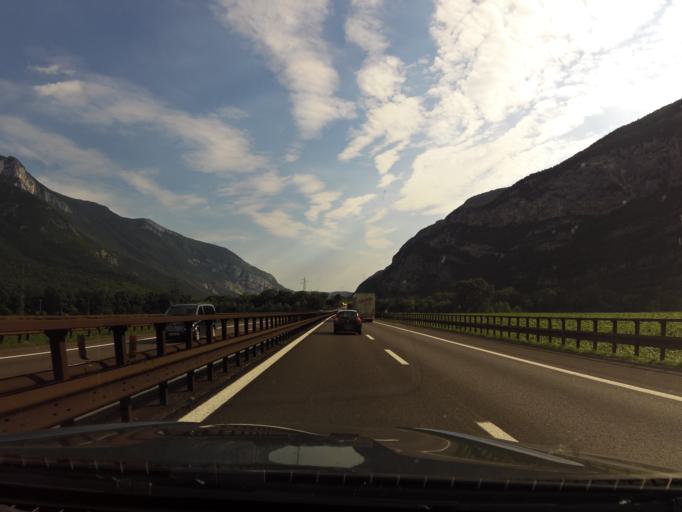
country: IT
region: Veneto
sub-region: Provincia di Verona
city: Dolce
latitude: 45.6228
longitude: 10.8631
